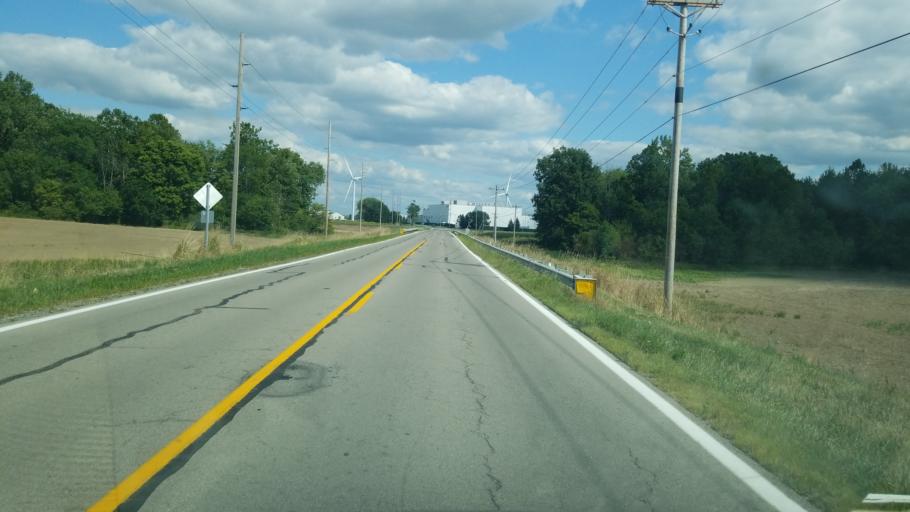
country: US
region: Ohio
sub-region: Logan County
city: Russells Point
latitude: 40.4519
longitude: -83.9090
